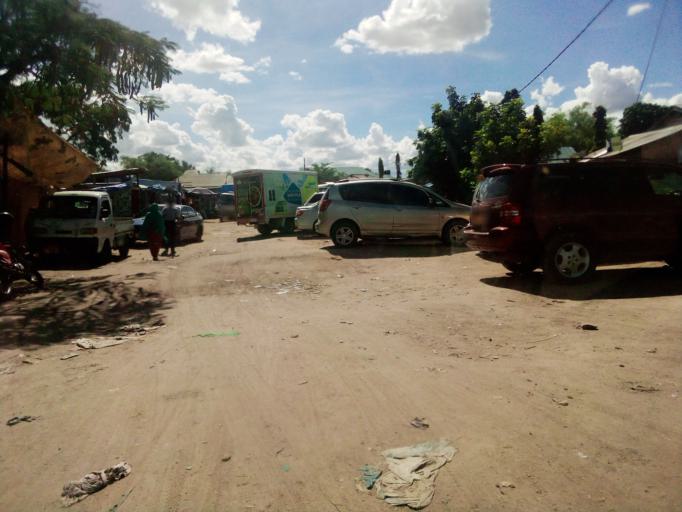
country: TZ
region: Dodoma
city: Dodoma
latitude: -6.1768
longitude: 35.7548
